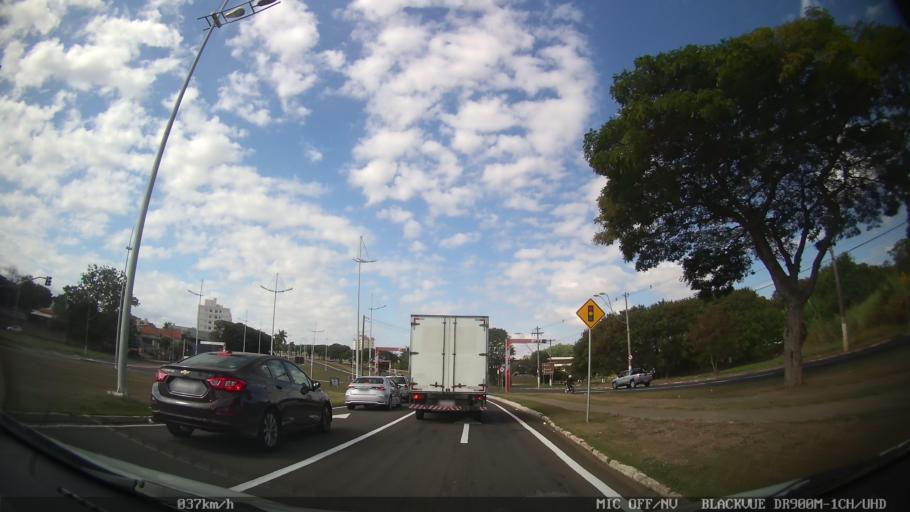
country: BR
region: Sao Paulo
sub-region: Americana
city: Americana
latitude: -22.7332
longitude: -47.3132
